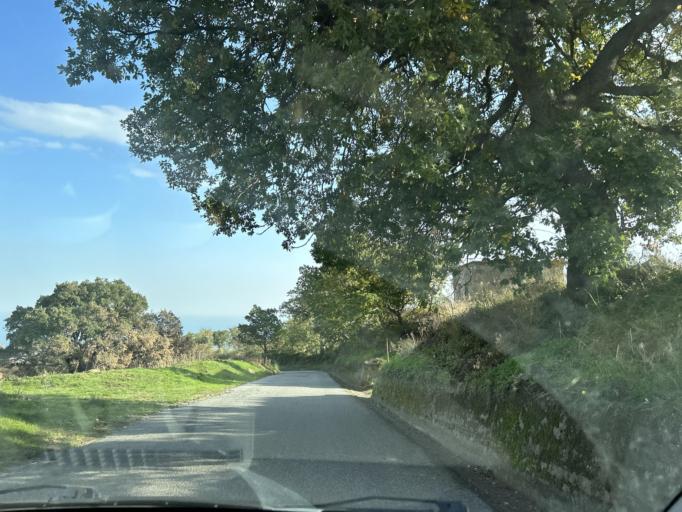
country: IT
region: Calabria
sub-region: Provincia di Catanzaro
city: Montepaone
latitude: 38.7163
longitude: 16.5123
